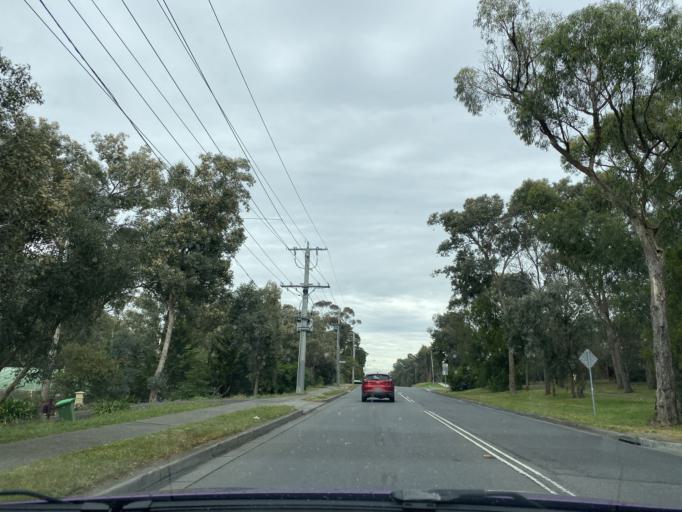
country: AU
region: Victoria
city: Saint Helena
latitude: -37.6865
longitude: 145.1362
